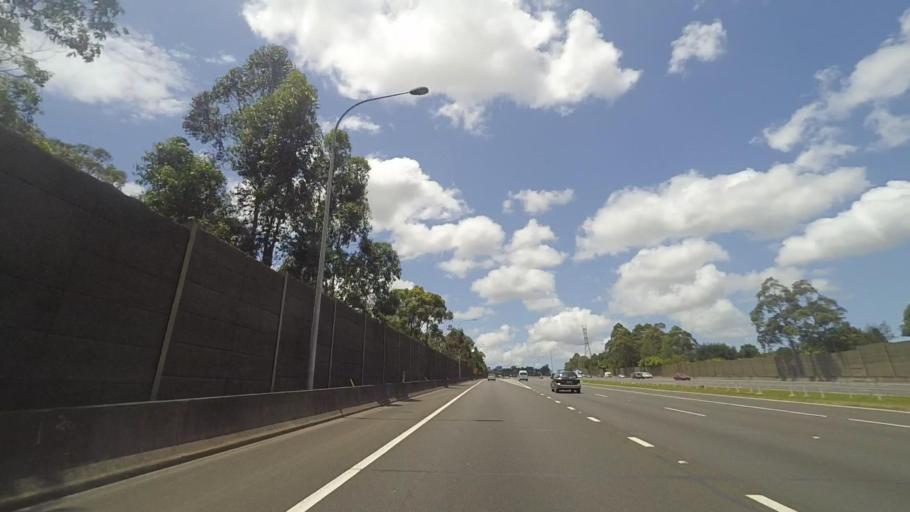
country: AU
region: New South Wales
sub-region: The Hills Shire
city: West Pennant
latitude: -33.7605
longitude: 151.0377
